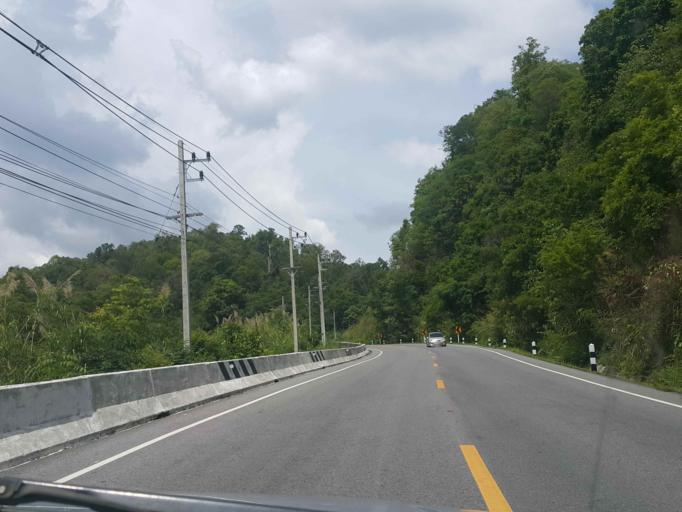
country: TH
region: Nan
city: Ban Luang
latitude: 18.8713
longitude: 100.4776
